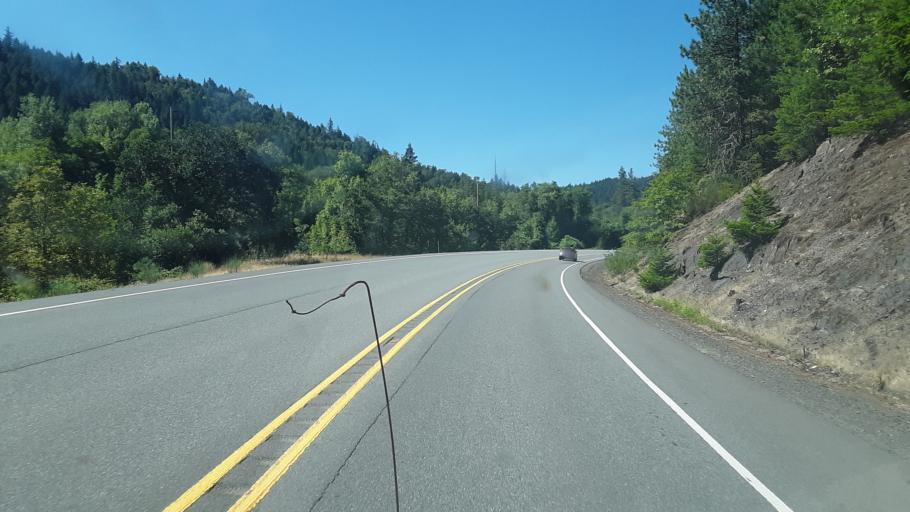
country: US
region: Oregon
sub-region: Josephine County
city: Redwood
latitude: 42.3736
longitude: -123.5001
